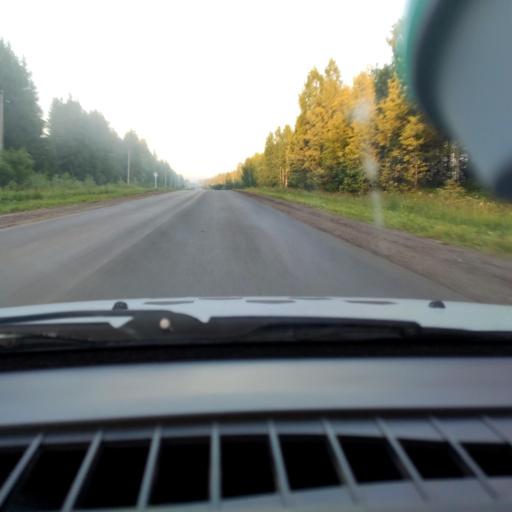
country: RU
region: Perm
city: Orda
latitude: 57.2235
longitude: 56.9553
